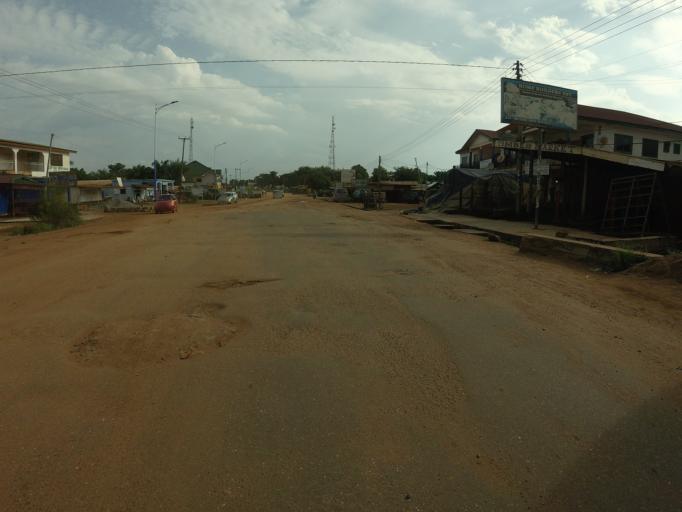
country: GH
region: Volta
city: Hohoe
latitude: 7.1489
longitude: 0.4678
